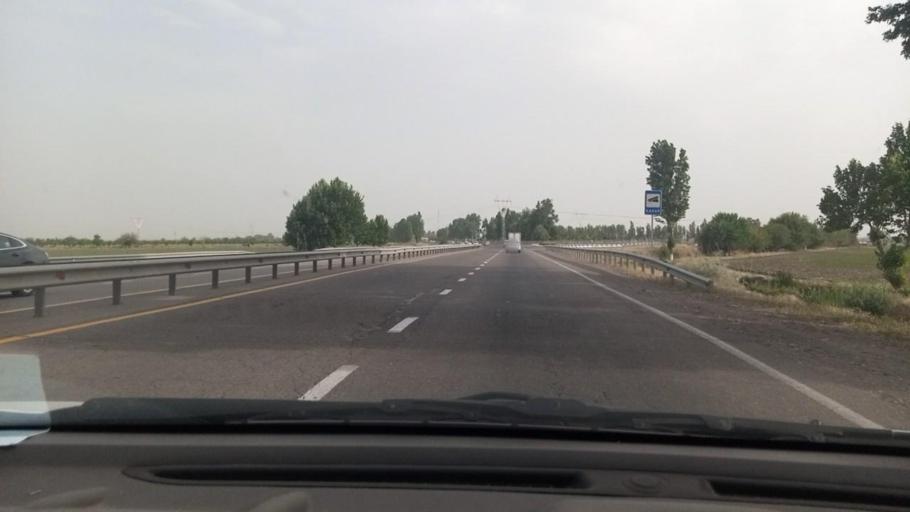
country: UZ
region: Toshkent Shahri
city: Bektemir
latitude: 41.1911
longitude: 69.4031
